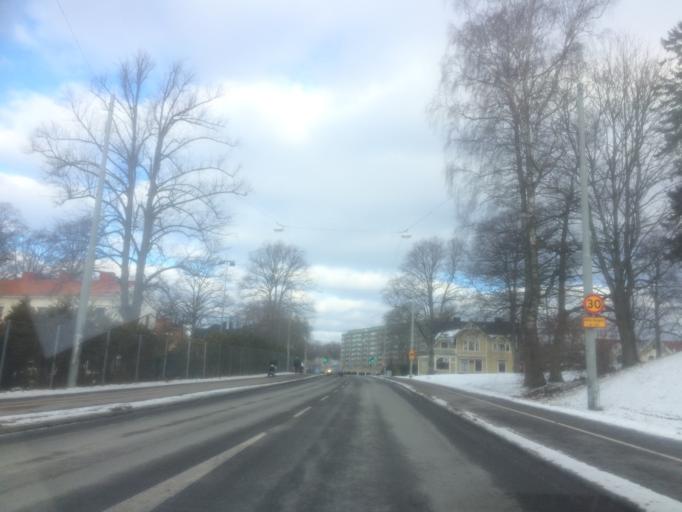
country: SE
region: Vaestra Goetaland
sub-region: Goteborg
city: Goeteborg
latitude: 57.7031
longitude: 12.0044
